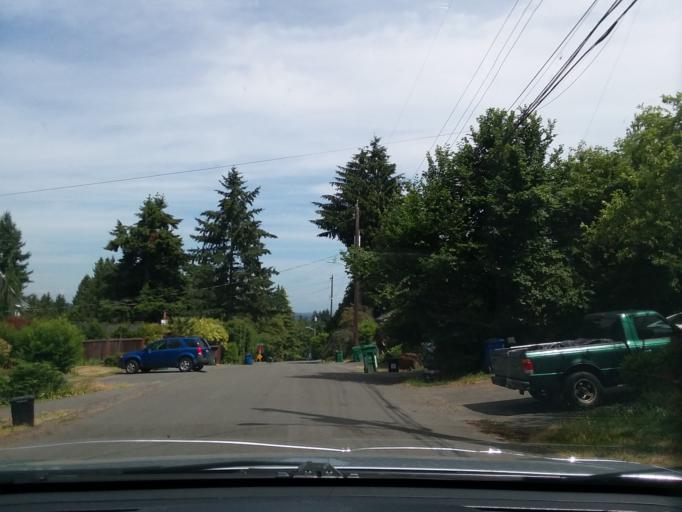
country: US
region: Washington
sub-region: King County
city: Shoreline
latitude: 47.7031
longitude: -122.3135
